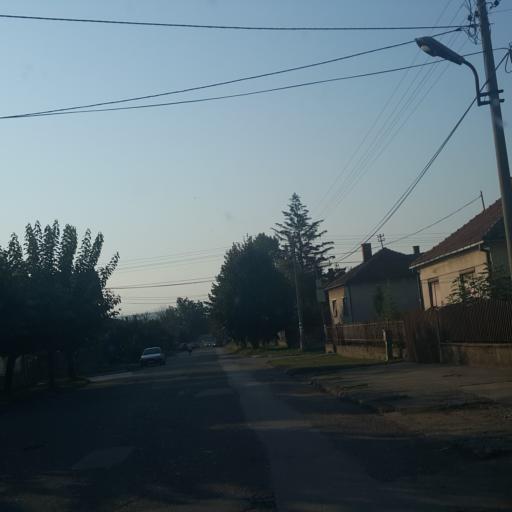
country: RS
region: Central Serbia
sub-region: Zajecarski Okrug
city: Zajecar
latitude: 43.9071
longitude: 22.2588
